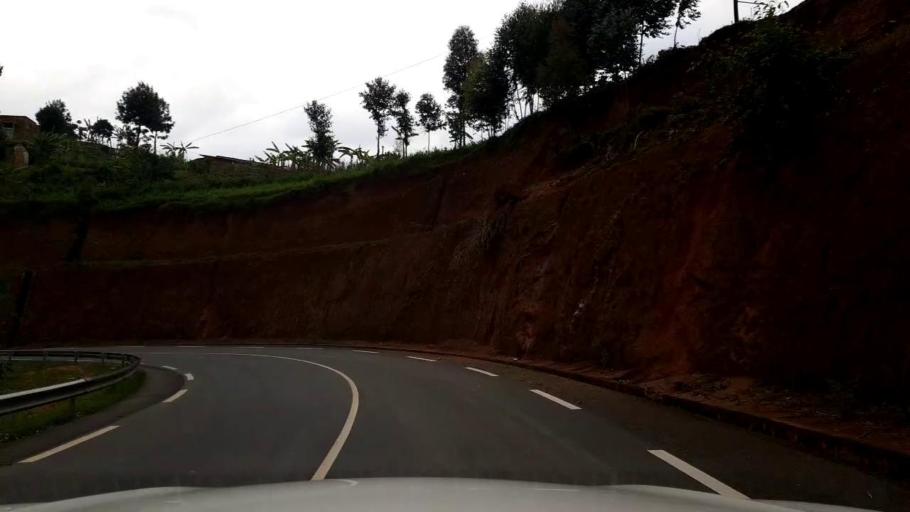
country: RW
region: Western Province
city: Kibuye
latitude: -1.8850
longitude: 29.3464
